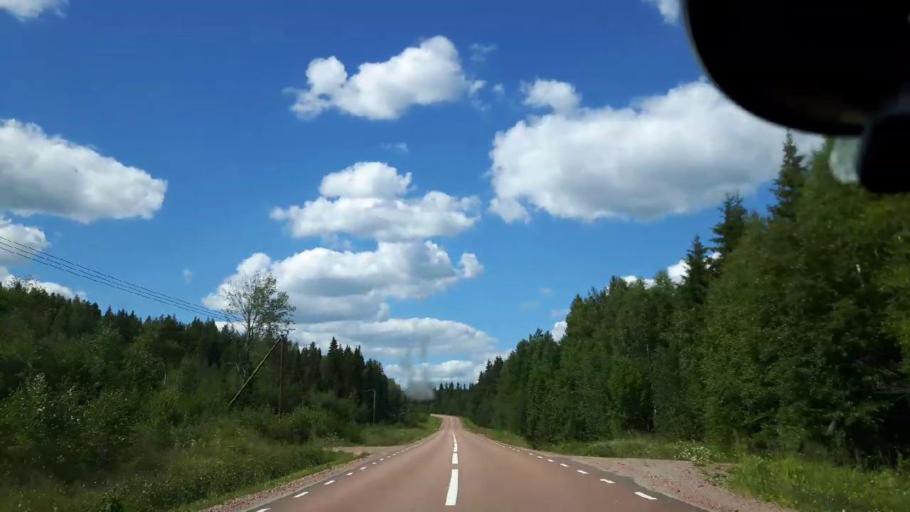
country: SE
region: Jaemtland
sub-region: Ragunda Kommun
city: Hammarstrand
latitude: 63.0159
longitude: 16.6183
